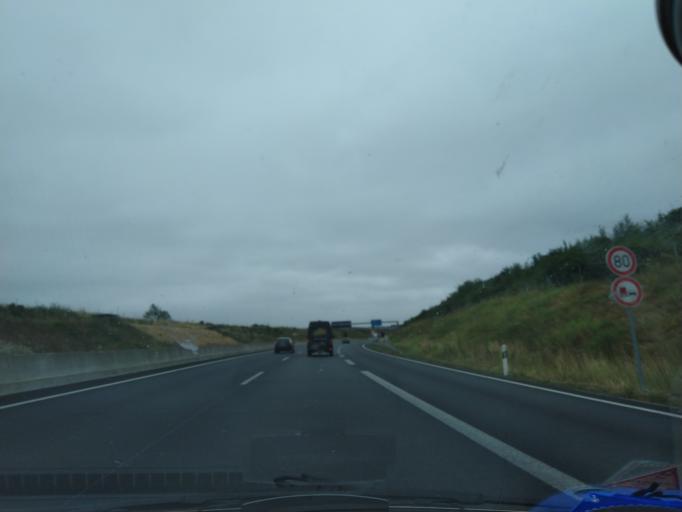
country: DE
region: North Rhine-Westphalia
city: Bad Oeynhausen
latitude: 52.2304
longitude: 8.8187
